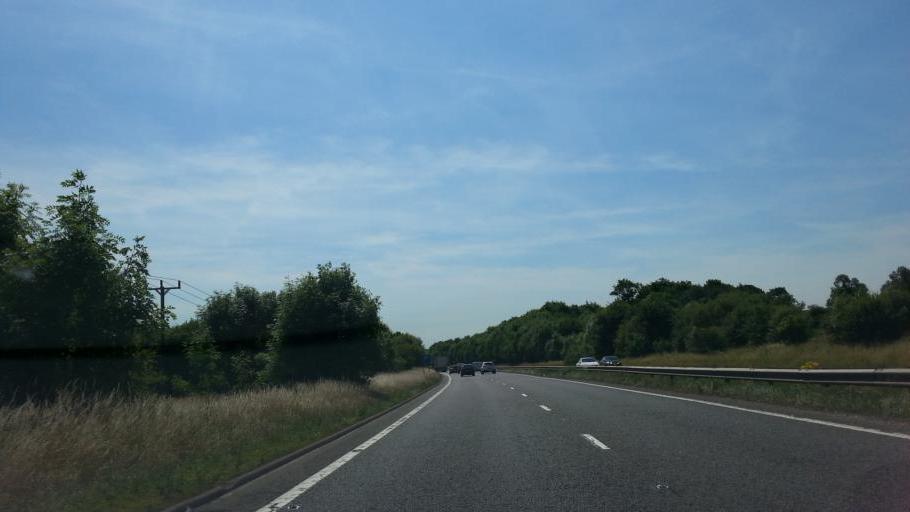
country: GB
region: England
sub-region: Derbyshire
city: Kilburn
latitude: 53.0261
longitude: -1.4429
